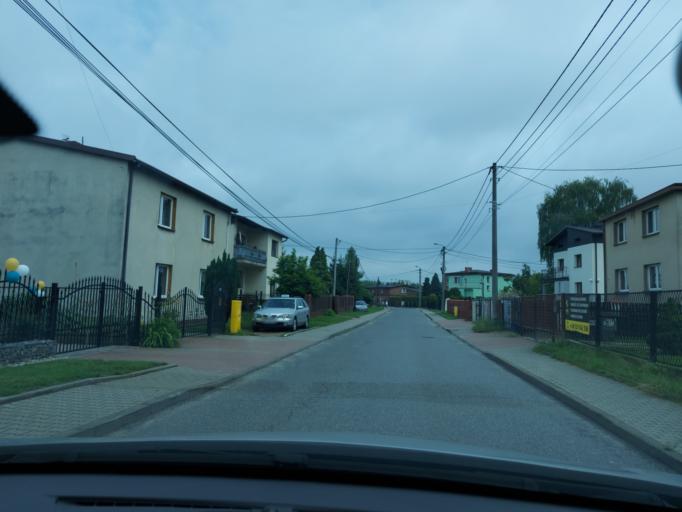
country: PL
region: Silesian Voivodeship
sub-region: Tychy
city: Tychy
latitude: 50.1096
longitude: 18.9547
